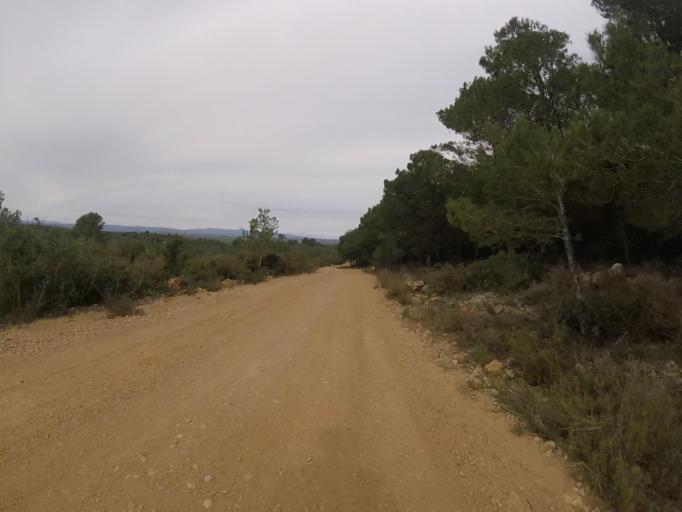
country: ES
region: Valencia
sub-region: Provincia de Castello
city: Benlloch
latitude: 40.1958
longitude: 0.0714
